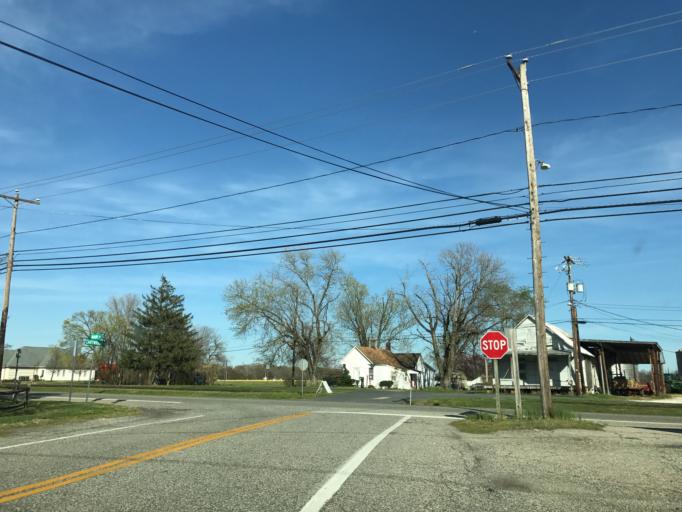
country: US
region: Maryland
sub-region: Caroline County
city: Greensboro
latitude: 39.0342
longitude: -75.7867
